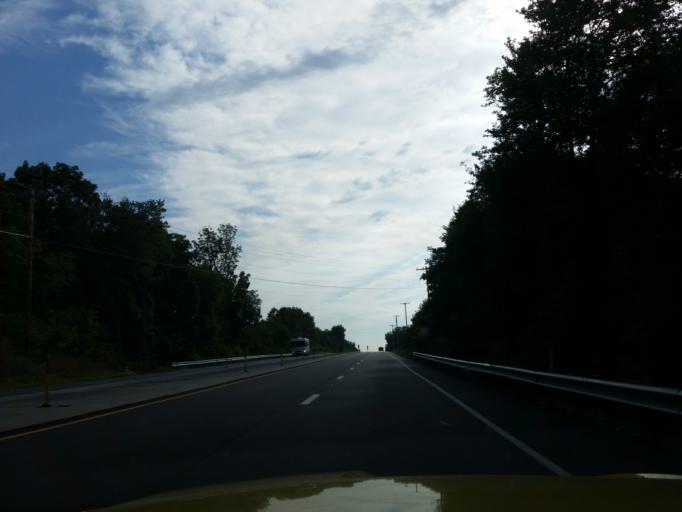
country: US
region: Pennsylvania
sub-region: Lebanon County
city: Jonestown
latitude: 40.4234
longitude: -76.4765
